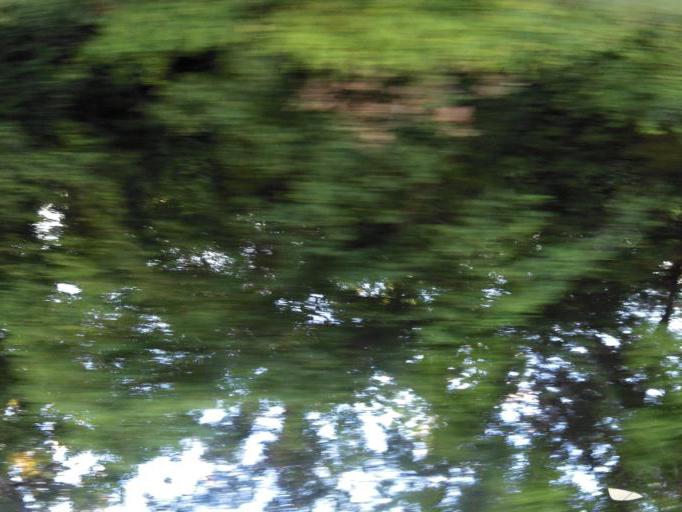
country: US
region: Missouri
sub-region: Jefferson County
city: Cedar Hill
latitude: 38.3337
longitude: -90.6671
